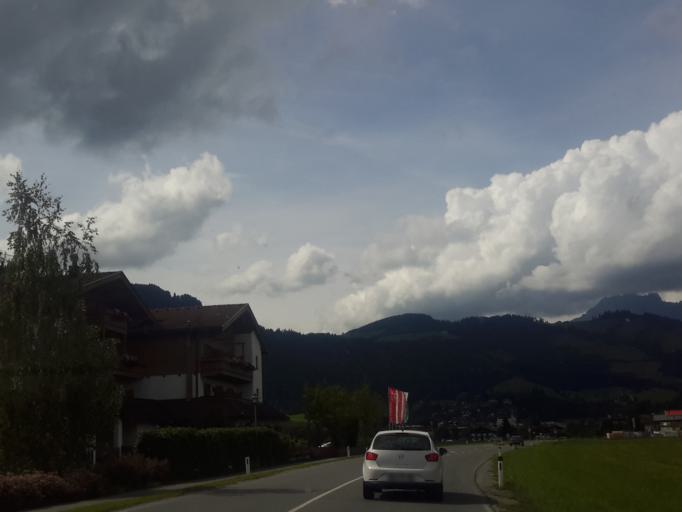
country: AT
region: Tyrol
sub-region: Politischer Bezirk Kitzbuhel
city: Reith bei Kitzbuhel
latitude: 47.4668
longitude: 12.3505
